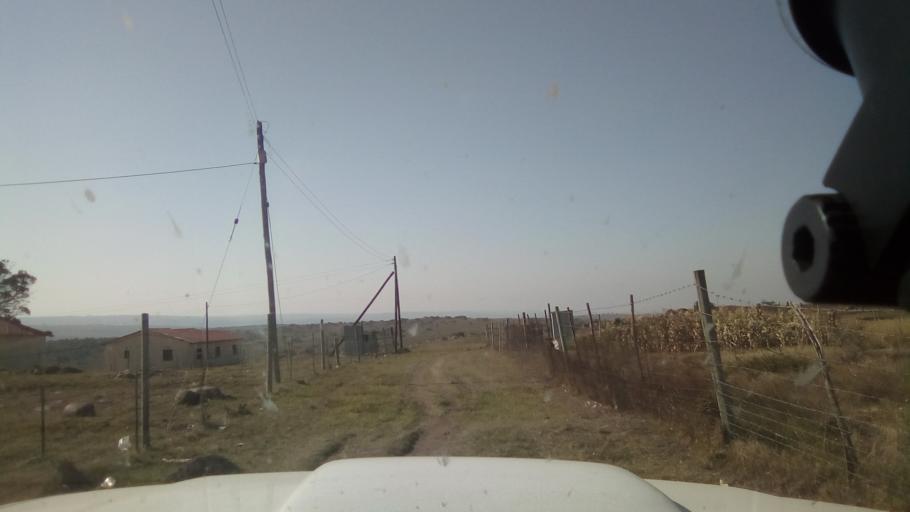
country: ZA
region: Eastern Cape
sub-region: Buffalo City Metropolitan Municipality
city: Bhisho
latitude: -32.9361
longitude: 27.3377
